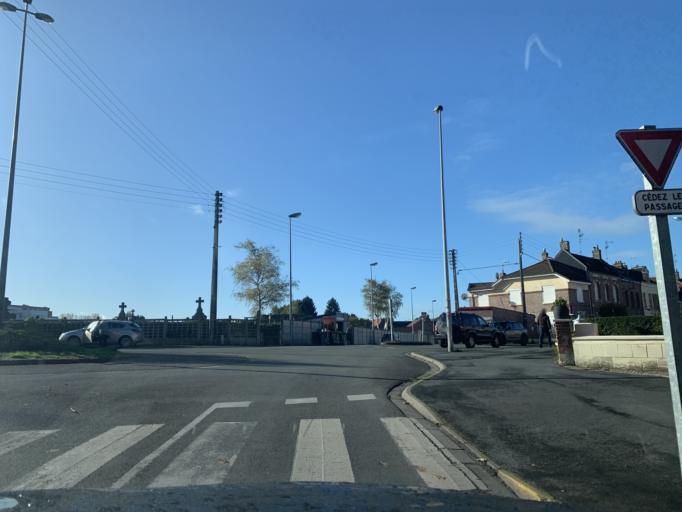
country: FR
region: Nord-Pas-de-Calais
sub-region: Departement du Nord
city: Cambrai
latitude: 50.1700
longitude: 3.2263
